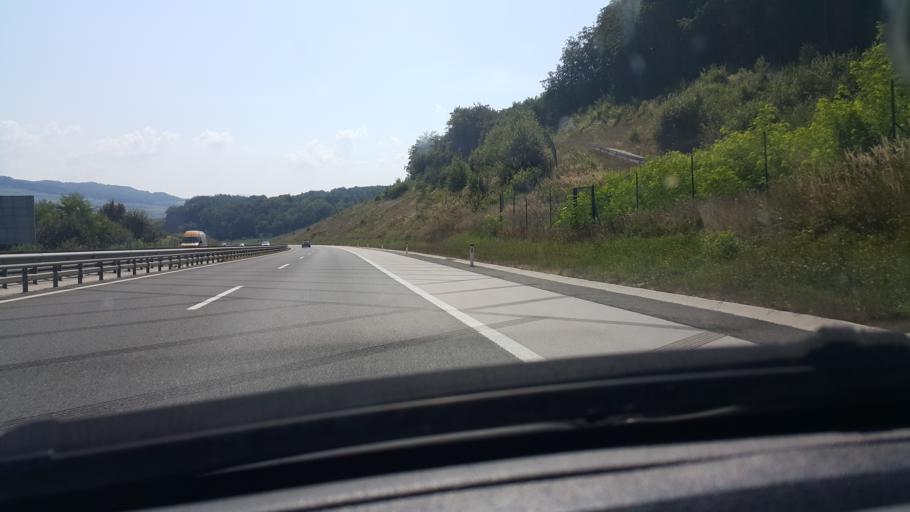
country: SI
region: Mirna Pec
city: Mirna Pec
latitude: 45.8712
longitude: 15.1111
